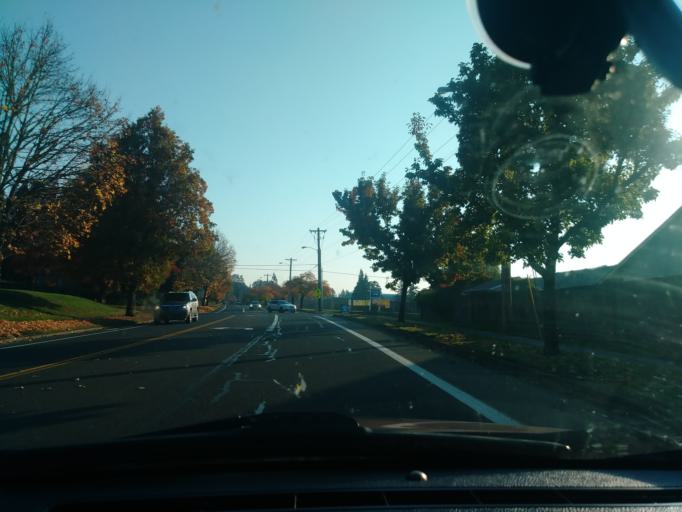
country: US
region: Oregon
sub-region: Washington County
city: Forest Grove
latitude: 45.5245
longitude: -123.1216
